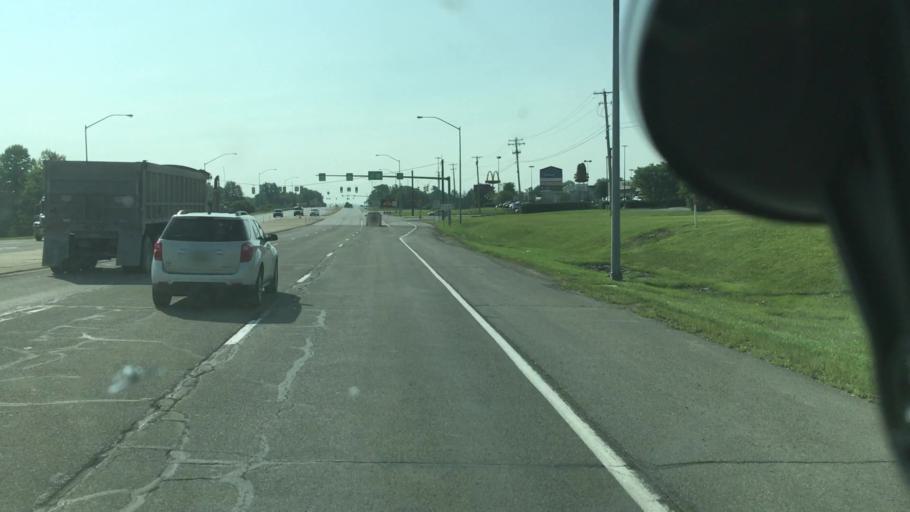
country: US
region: Pennsylvania
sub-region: Lawrence County
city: Oakwood
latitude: 41.0126
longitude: -80.3959
